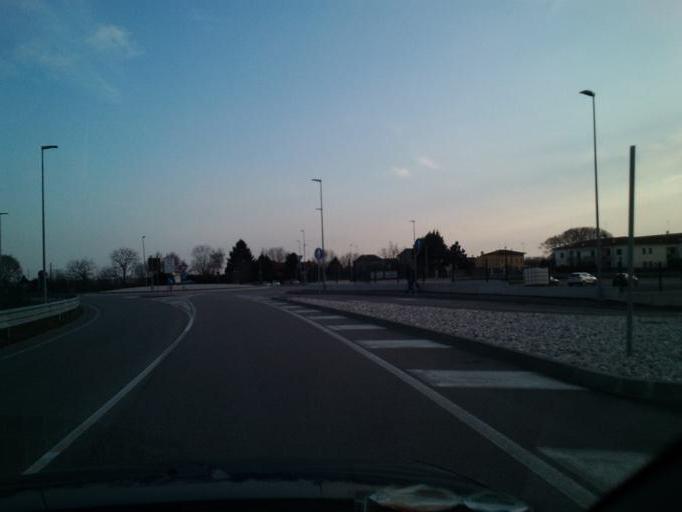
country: IT
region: Veneto
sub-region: Provincia di Verona
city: Dossobuono
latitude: 45.3992
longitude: 10.9021
